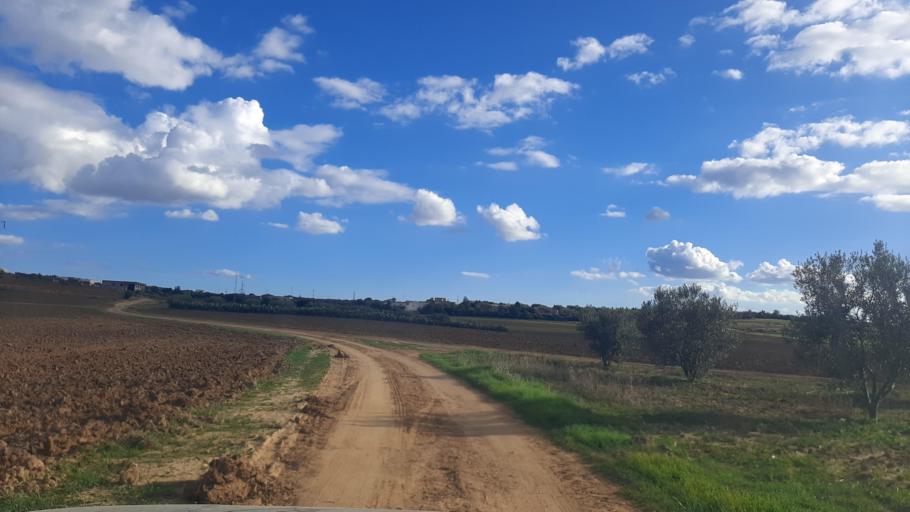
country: TN
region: Nabul
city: Bu `Urqub
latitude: 36.4456
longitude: 10.5028
